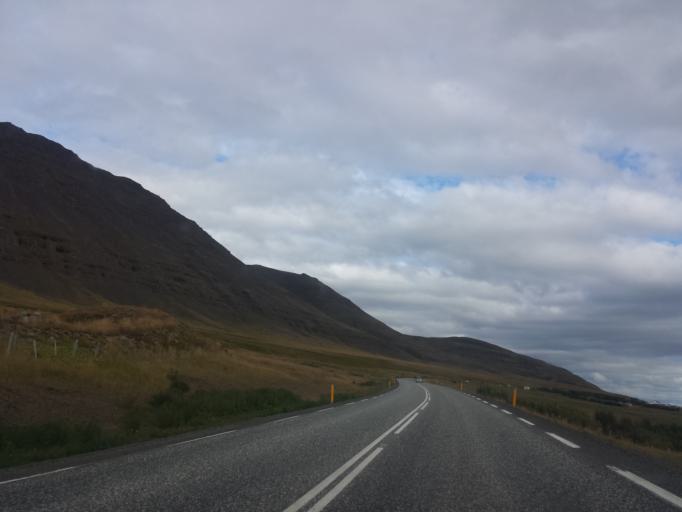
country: IS
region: Capital Region
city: Reykjavik
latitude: 64.3167
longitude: -21.8866
